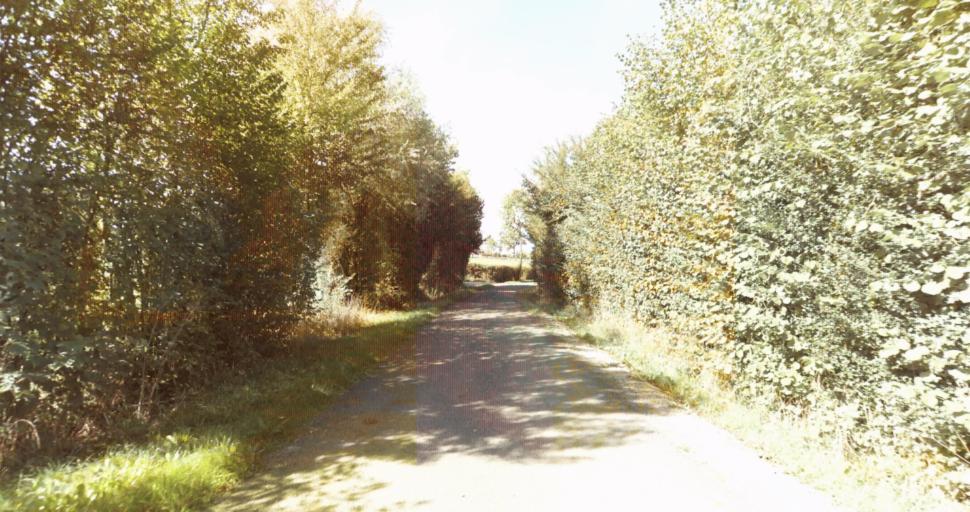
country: FR
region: Lower Normandy
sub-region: Departement de l'Orne
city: Gace
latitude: 48.7414
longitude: 0.2605
